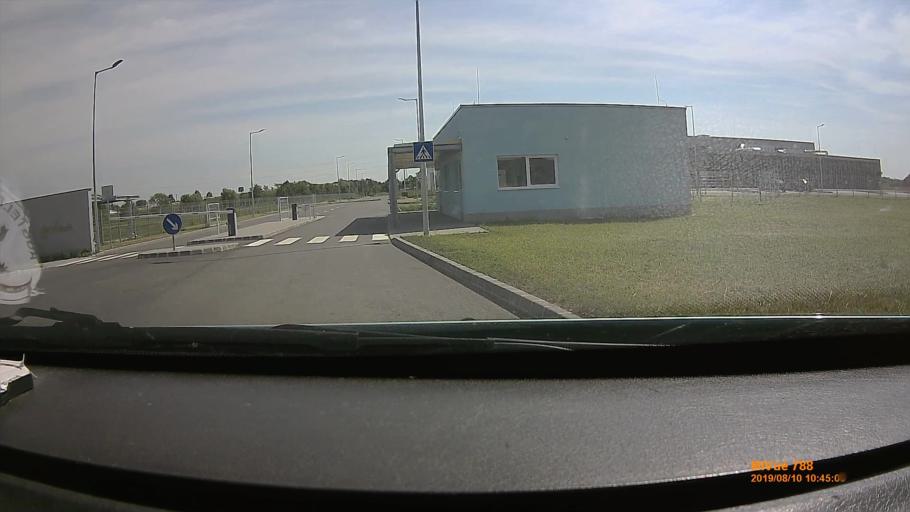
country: HU
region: Borsod-Abauj-Zemplen
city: Malyi
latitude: 48.0540
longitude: 20.8099
